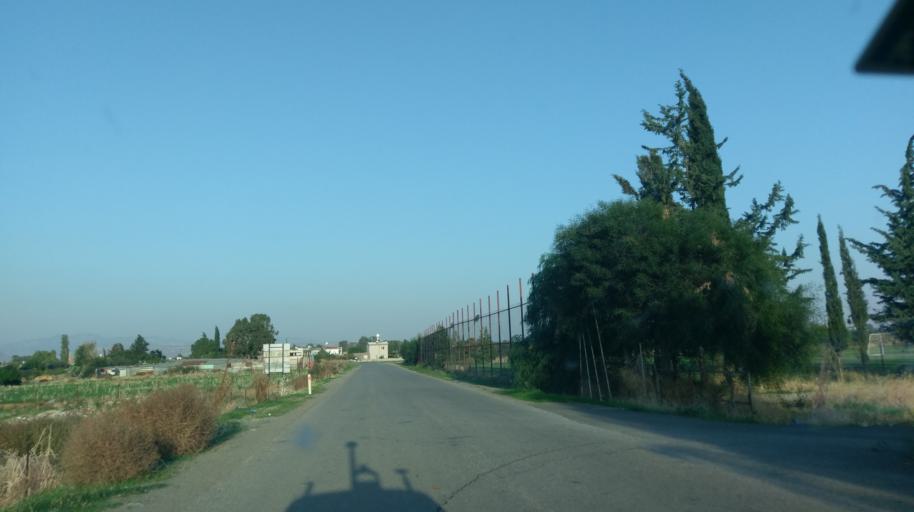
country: CY
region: Lefkosia
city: Morfou
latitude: 35.1610
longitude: 33.0031
